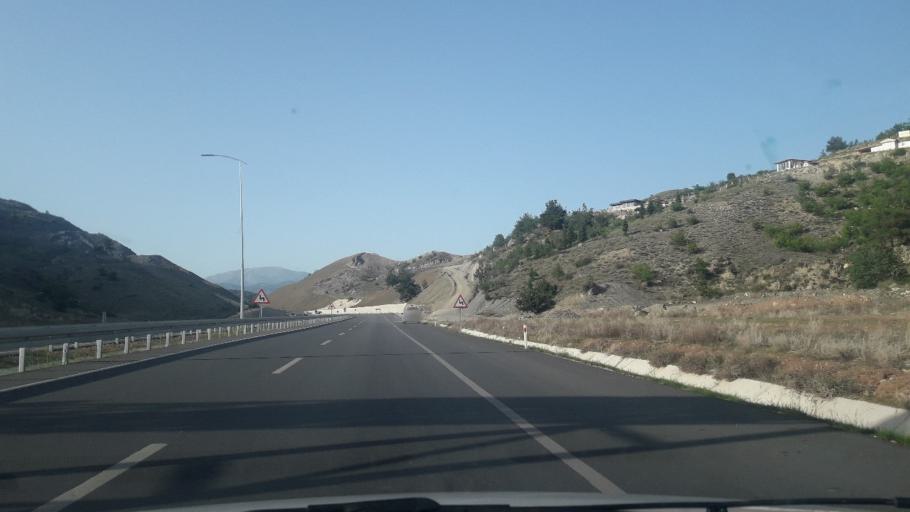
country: TR
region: Amasya
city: Amasya
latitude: 40.6658
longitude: 35.7984
